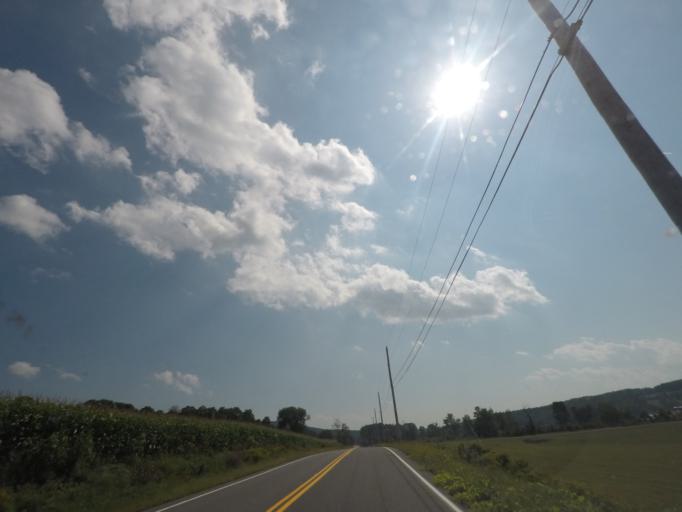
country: US
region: New York
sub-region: Rensselaer County
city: Poestenkill
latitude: 42.7915
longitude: -73.5322
